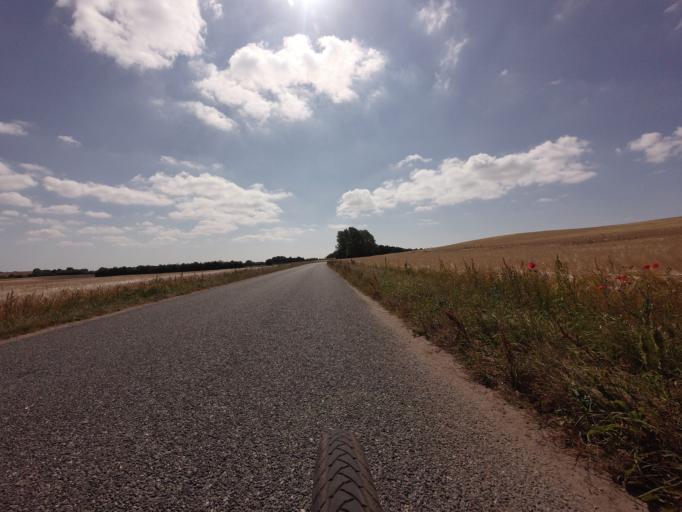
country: DK
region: Central Jutland
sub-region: Odder Kommune
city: Odder
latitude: 55.9133
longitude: 10.0585
